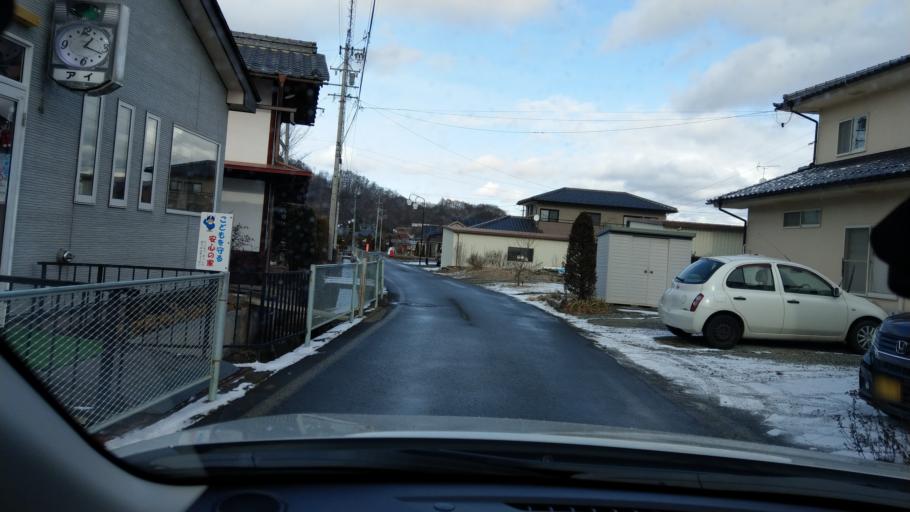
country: JP
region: Nagano
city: Saku
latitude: 36.1624
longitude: 138.4792
